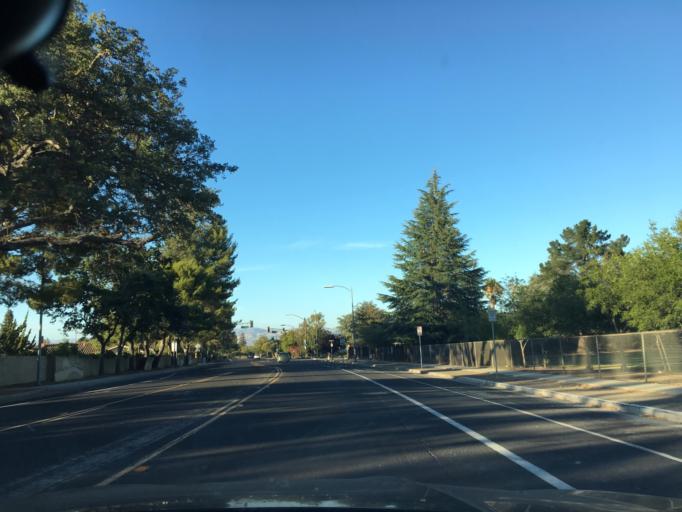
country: US
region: California
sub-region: Santa Clara County
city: Cambrian Park
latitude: 37.2295
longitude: -121.8979
